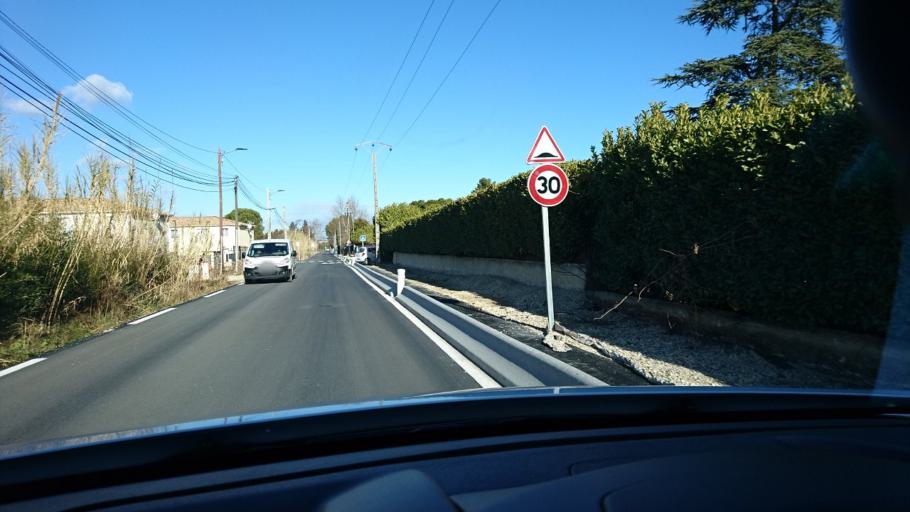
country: FR
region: Provence-Alpes-Cote d'Azur
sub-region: Departement du Vaucluse
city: Morieres-les-Avignon
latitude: 43.9258
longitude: 4.9055
